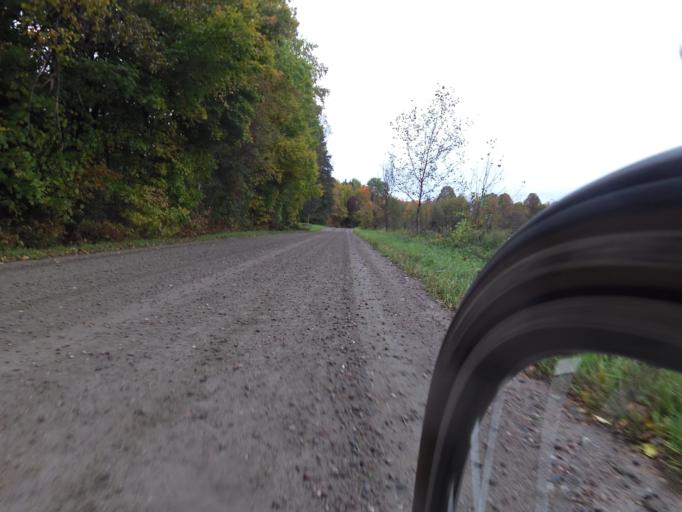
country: CA
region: Quebec
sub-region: Outaouais
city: Shawville
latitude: 45.6874
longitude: -76.5642
